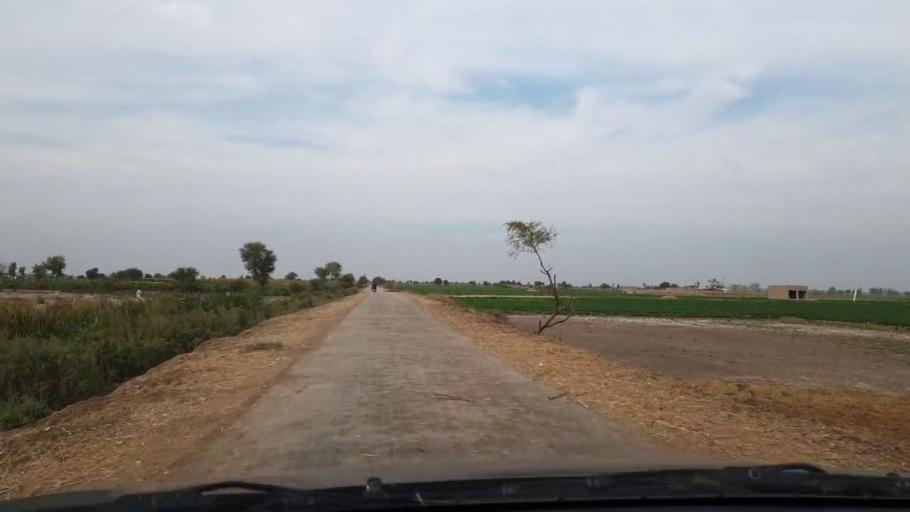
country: PK
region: Sindh
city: Khadro
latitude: 26.1622
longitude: 68.7302
